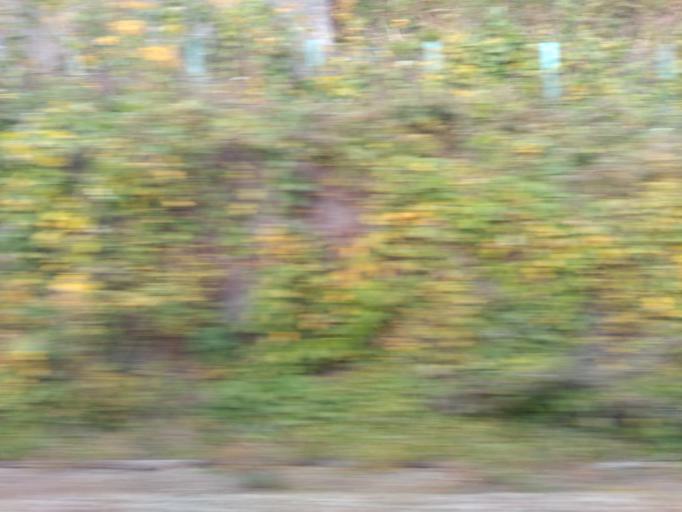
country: JP
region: Hokkaido
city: Niseko Town
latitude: 42.5878
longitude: 140.6818
